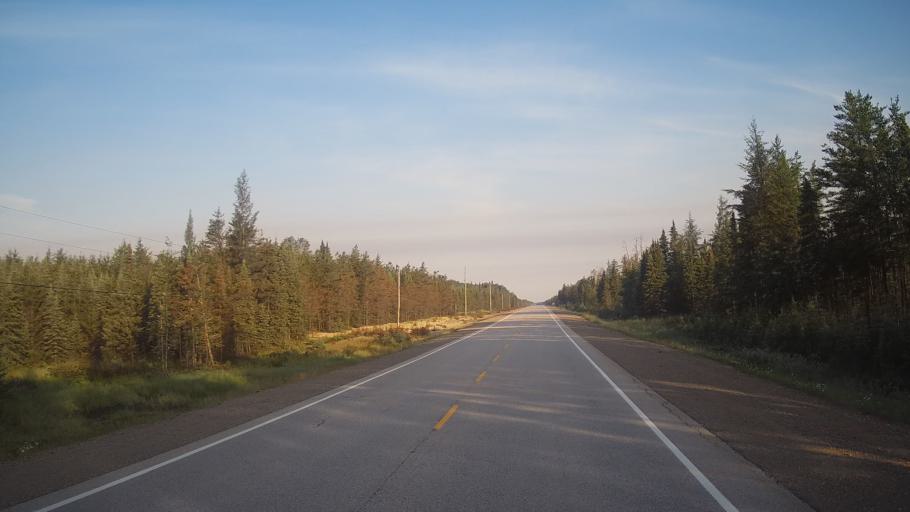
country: CA
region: Ontario
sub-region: Rainy River District
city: Atikokan
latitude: 49.2354
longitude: -90.9801
